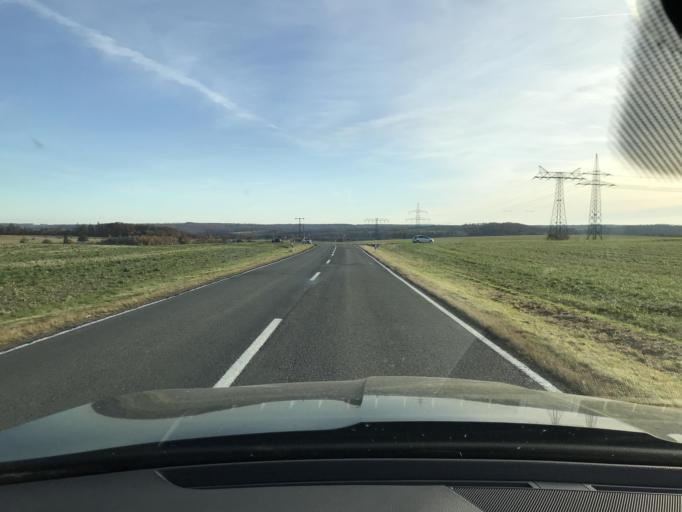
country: DE
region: Saxony-Anhalt
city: Huttenrode
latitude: 51.7619
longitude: 10.9048
